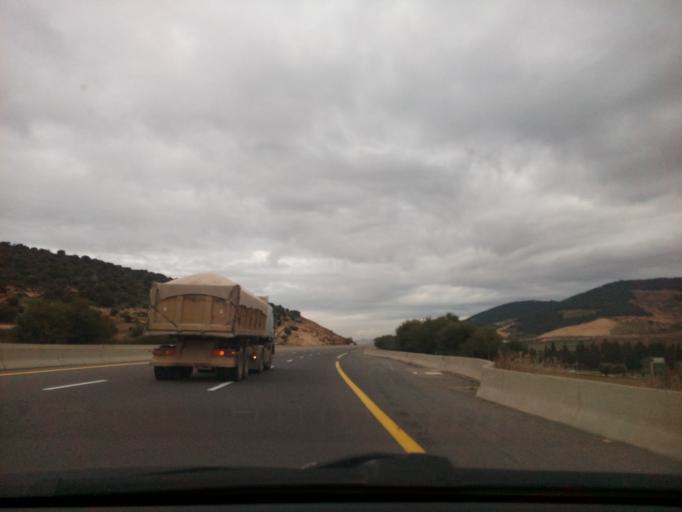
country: DZ
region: Sidi Bel Abbes
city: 'Ain el Berd
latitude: 35.4094
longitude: -0.4889
